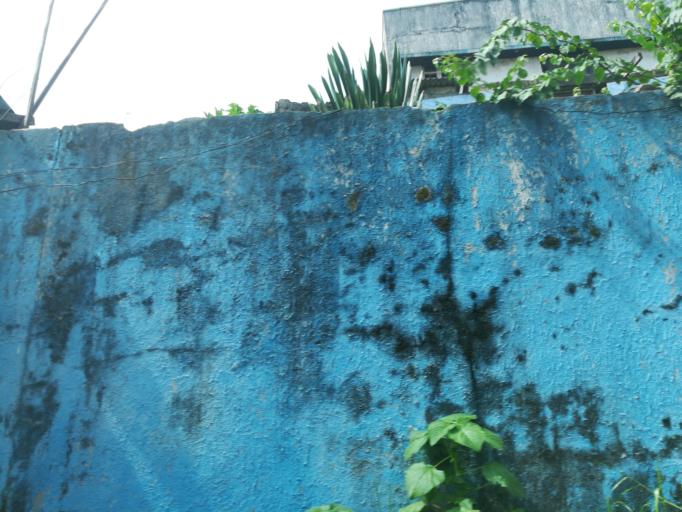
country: NG
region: Lagos
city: Oshodi
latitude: 6.5448
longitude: 3.3217
